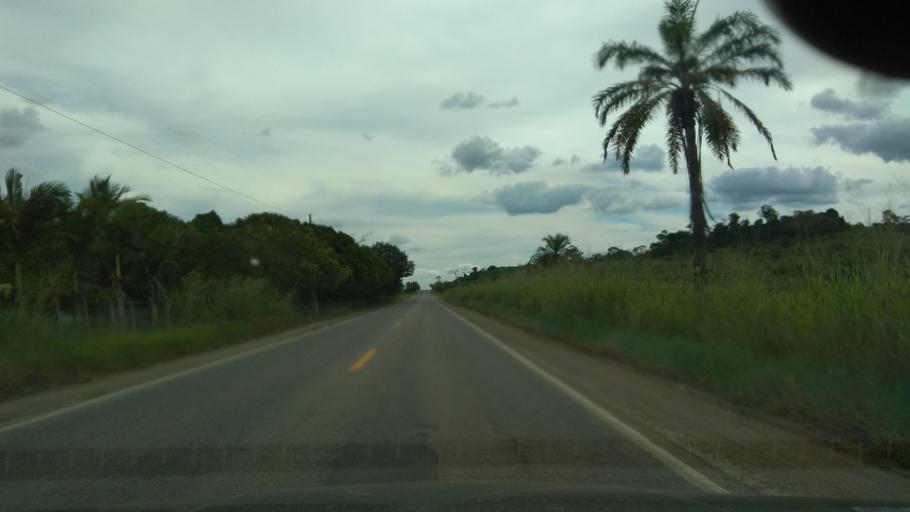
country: BR
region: Bahia
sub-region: Ipiau
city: Ipiau
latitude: -14.1462
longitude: -39.7086
